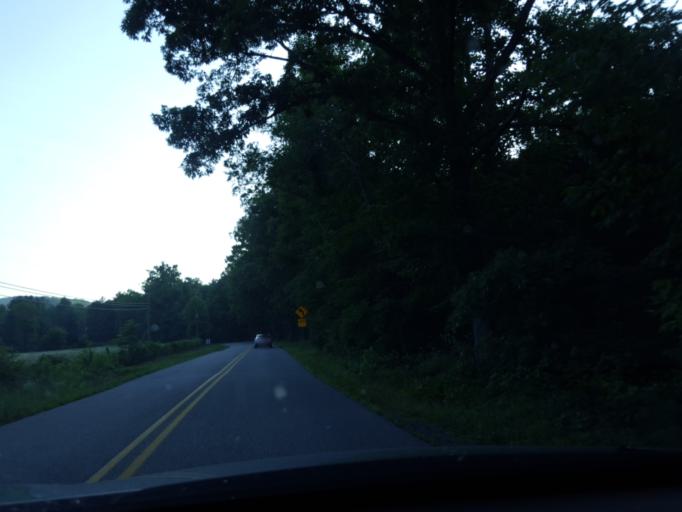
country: US
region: Virginia
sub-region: Augusta County
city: Lyndhurst
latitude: 37.9328
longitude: -78.9751
